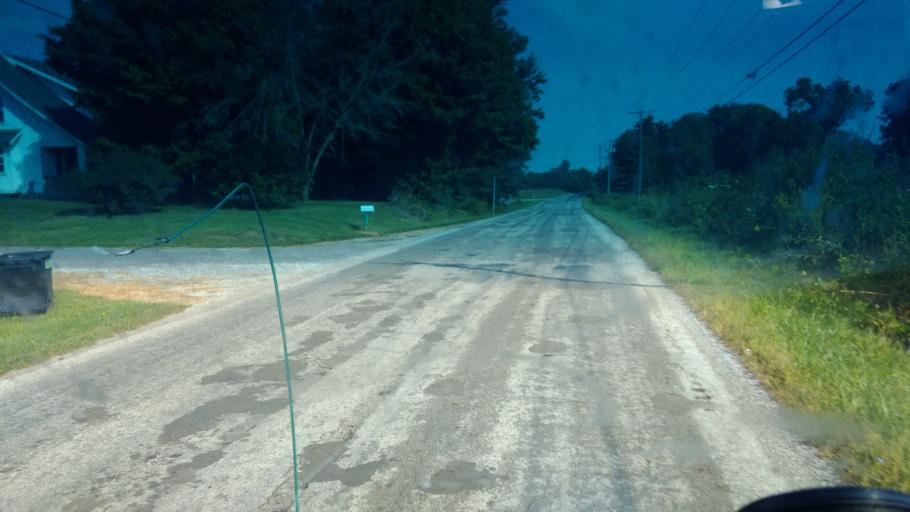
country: US
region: Ohio
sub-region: Morrow County
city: Mount Gilead
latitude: 40.5846
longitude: -82.8618
